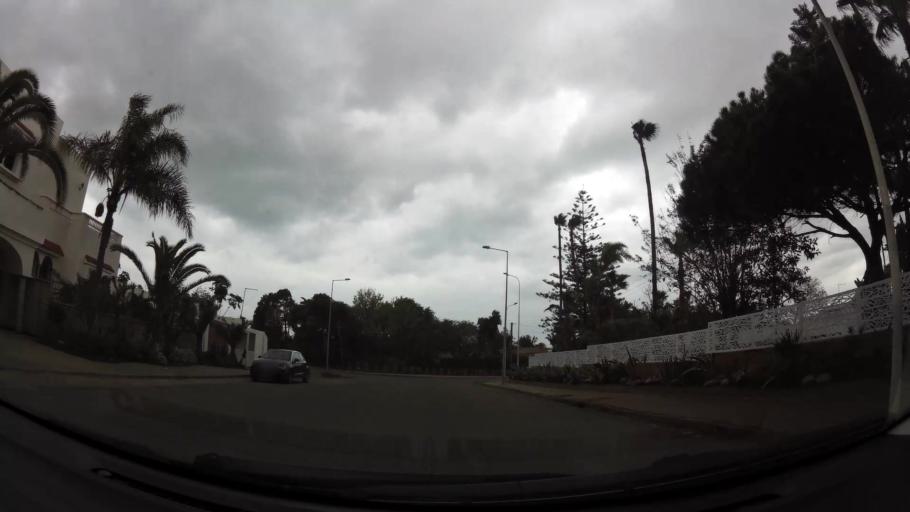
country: MA
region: Grand Casablanca
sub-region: Casablanca
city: Casablanca
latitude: 33.5822
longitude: -7.6695
